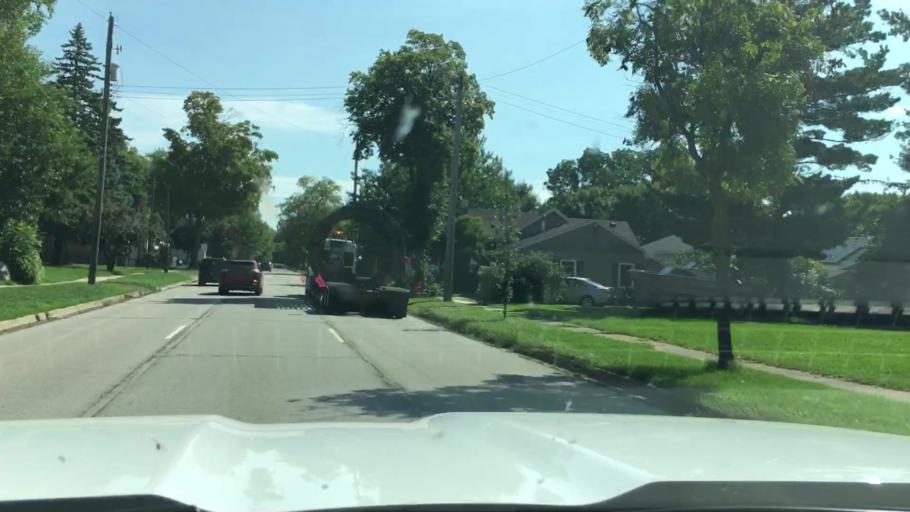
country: US
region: Michigan
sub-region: Bay County
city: Bay City
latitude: 43.5974
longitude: -83.9131
